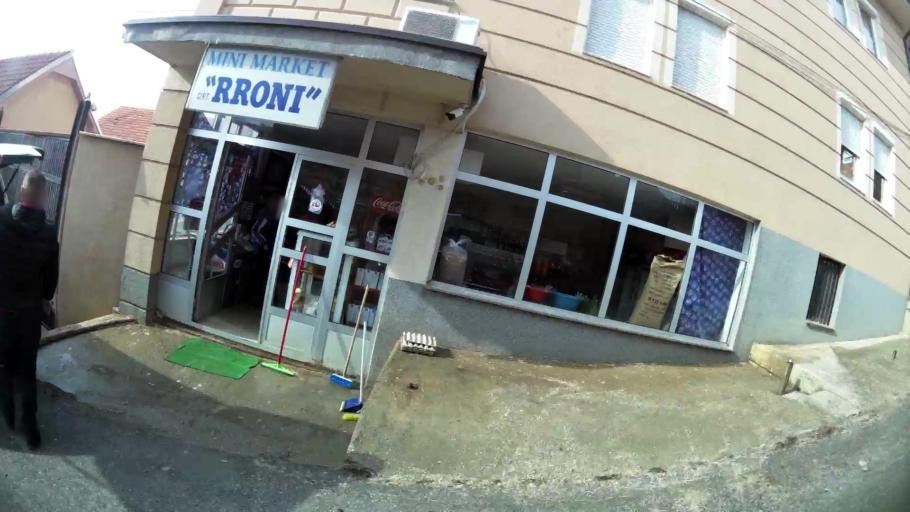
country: XK
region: Pristina
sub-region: Komuna e Prishtines
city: Pristina
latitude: 42.6840
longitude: 21.1699
